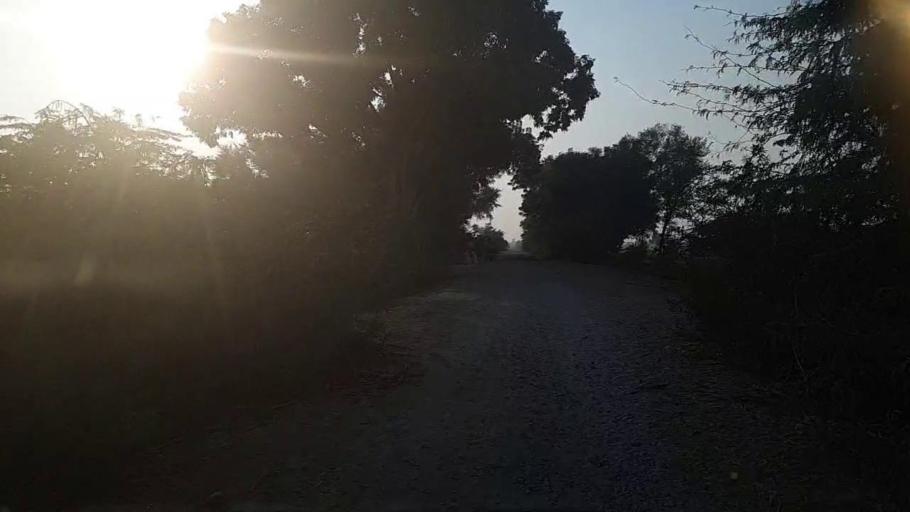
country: PK
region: Sindh
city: Pad Idan
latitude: 26.7192
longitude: 68.4266
